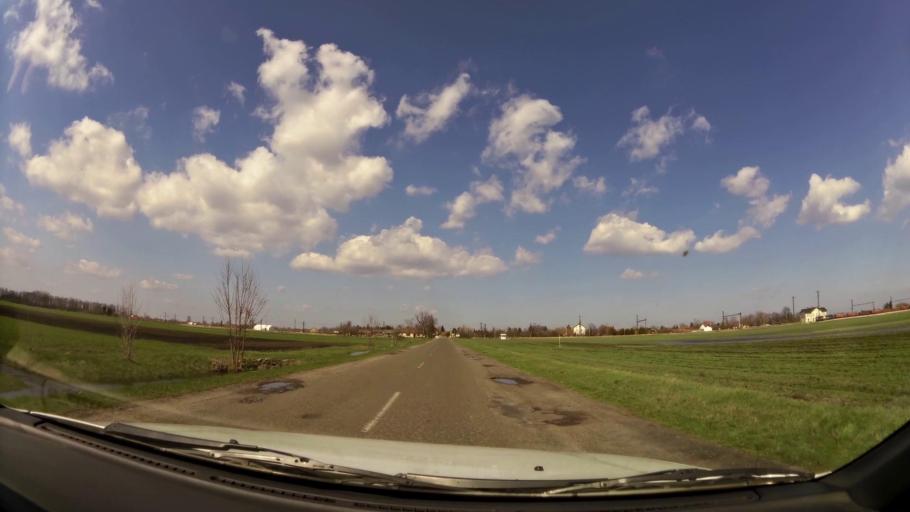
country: HU
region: Pest
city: Tapiogyorgye
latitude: 47.3229
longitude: 19.9462
